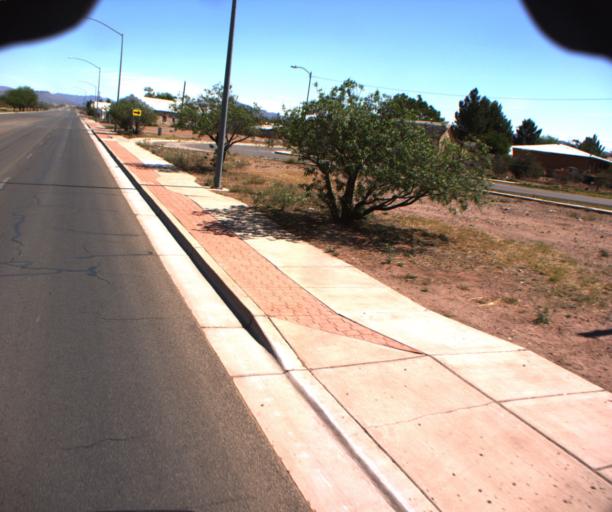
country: US
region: Arizona
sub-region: Cochise County
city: Douglas
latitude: 31.3532
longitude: -109.5518
